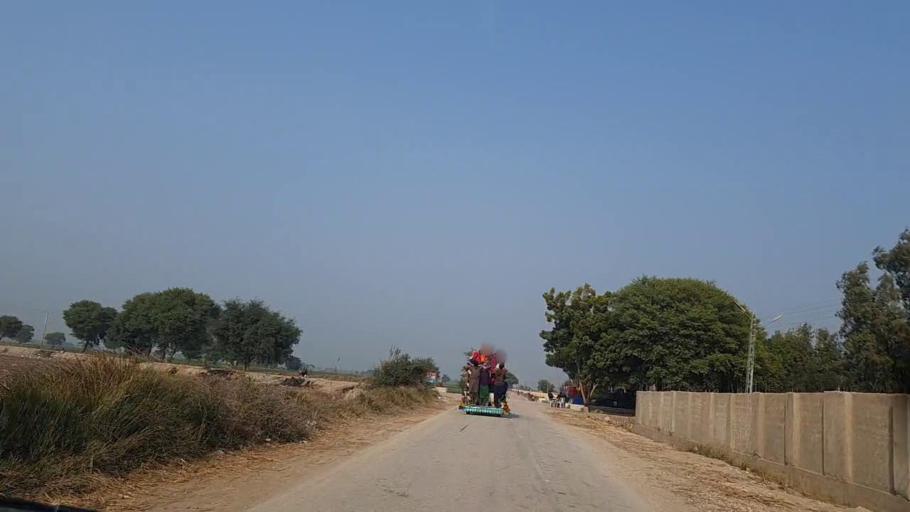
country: PK
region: Sindh
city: Sann
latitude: 26.1819
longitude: 68.1095
